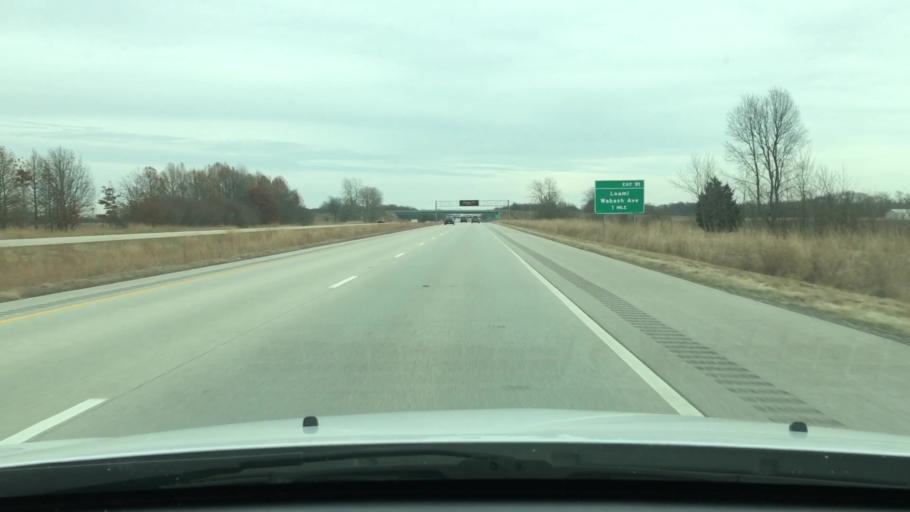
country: US
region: Illinois
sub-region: Sangamon County
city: Jerome
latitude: 39.7517
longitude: -89.7779
